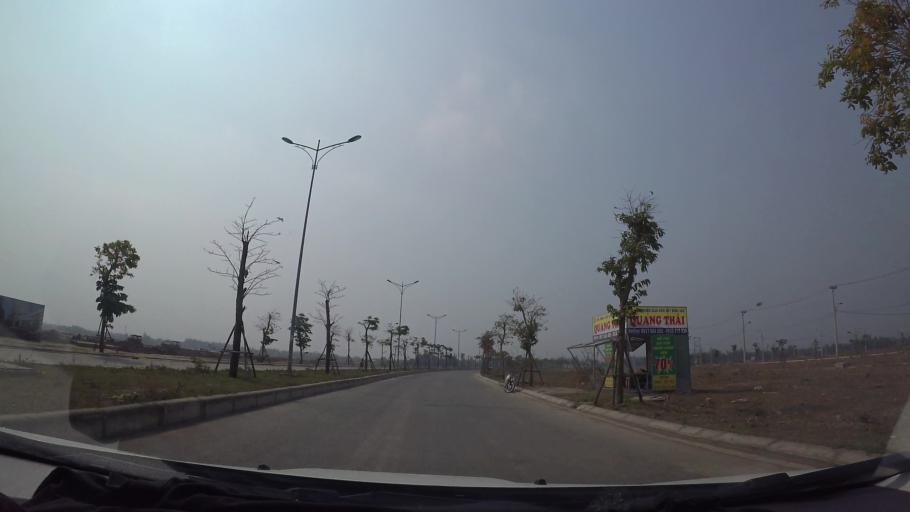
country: VN
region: Da Nang
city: Ngu Hanh Son
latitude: 15.9991
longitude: 108.2476
